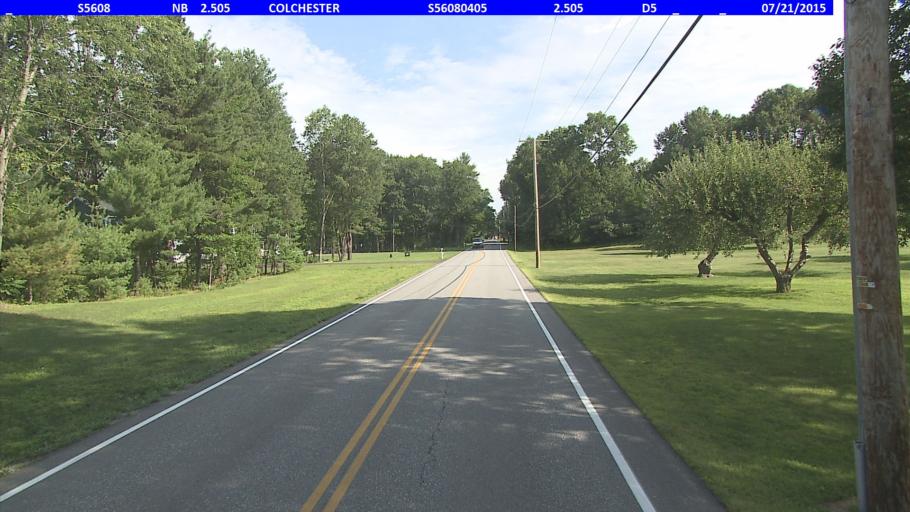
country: US
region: Vermont
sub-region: Chittenden County
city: Winooski
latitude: 44.5328
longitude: -73.2081
